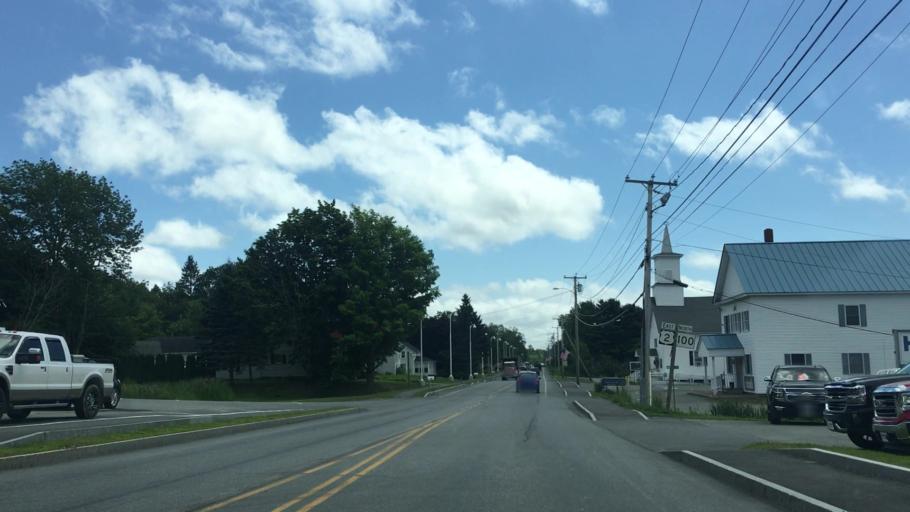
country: US
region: Maine
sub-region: Penobscot County
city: Hermon
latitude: 44.8097
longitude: -68.9107
